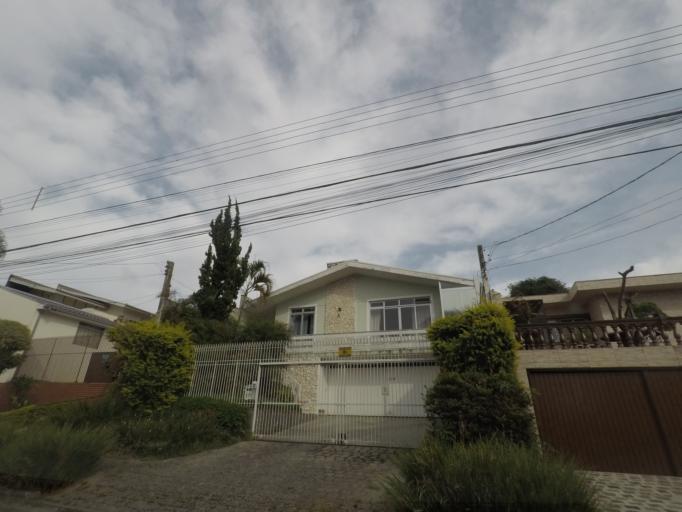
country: BR
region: Parana
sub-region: Curitiba
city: Curitiba
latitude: -25.4072
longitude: -49.2738
